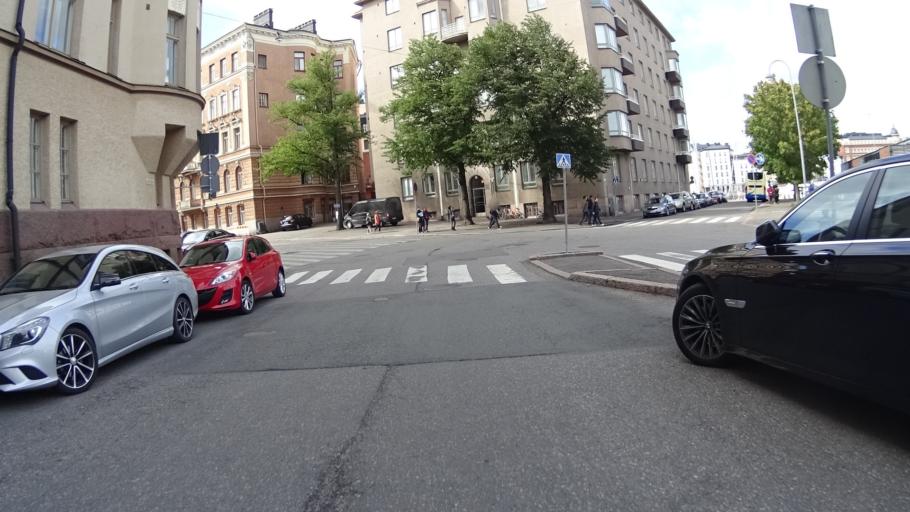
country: FI
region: Uusimaa
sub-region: Helsinki
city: Helsinki
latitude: 60.1688
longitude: 24.9640
